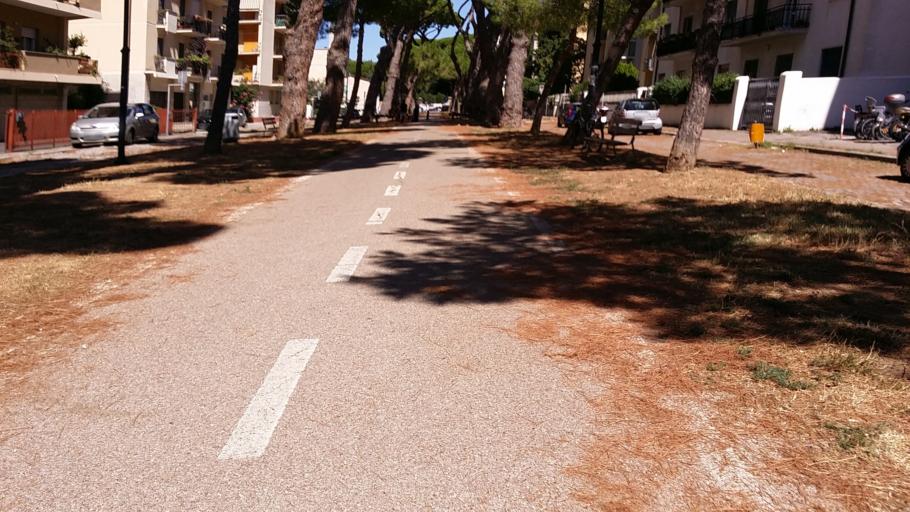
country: IT
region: Tuscany
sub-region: Provincia di Livorno
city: Livorno
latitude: 43.5344
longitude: 10.3193
